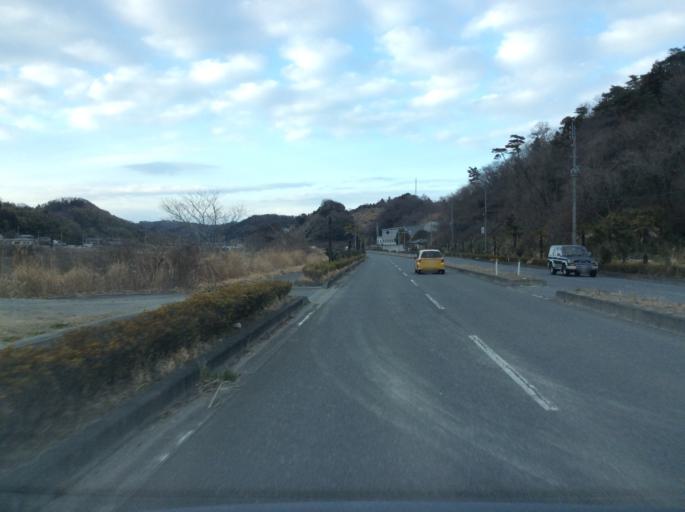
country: JP
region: Fukushima
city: Iwaki
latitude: 36.9602
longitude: 140.9194
